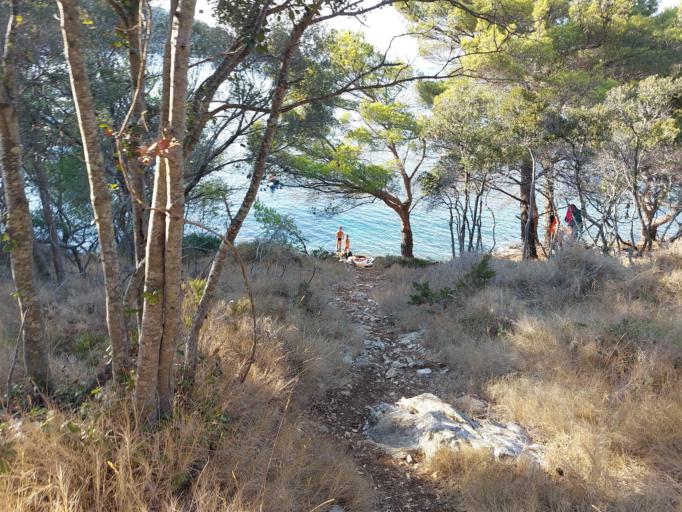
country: HR
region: Dubrovacko-Neretvanska
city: Smokvica
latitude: 42.7652
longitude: 16.8013
